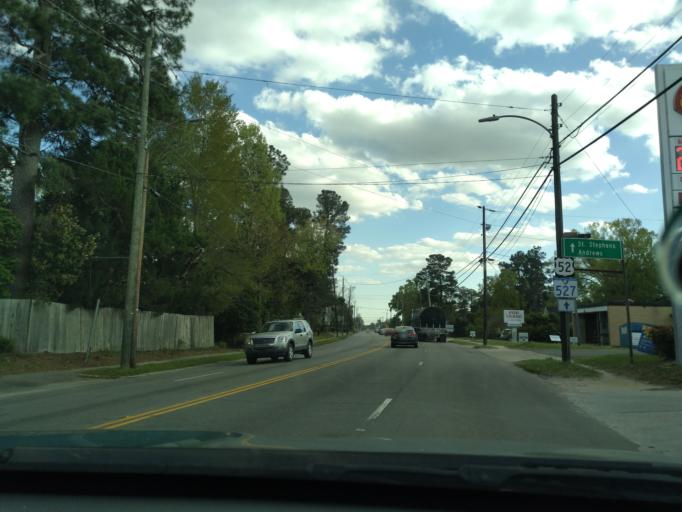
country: US
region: South Carolina
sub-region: Williamsburg County
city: Kingstree
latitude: 33.6712
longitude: -79.8360
